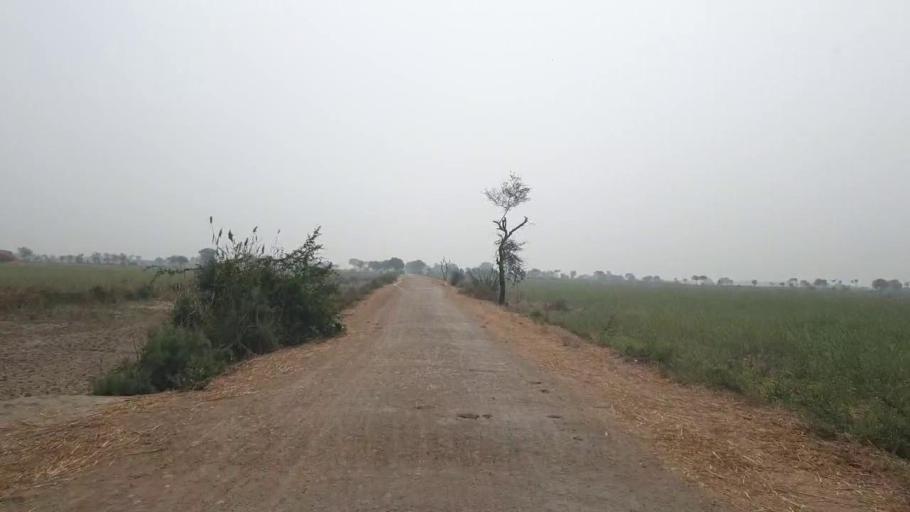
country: PK
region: Sindh
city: Kario
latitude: 24.6494
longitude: 68.6217
